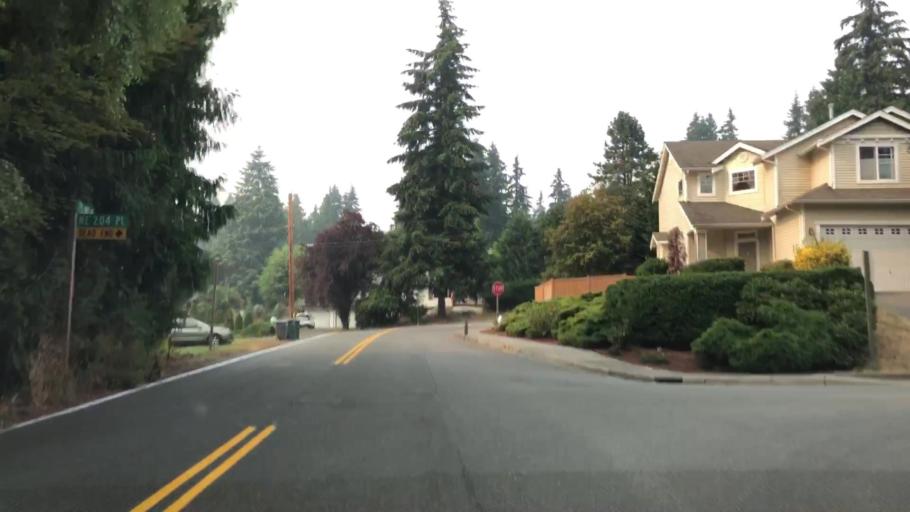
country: US
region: Washington
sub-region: King County
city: Kenmore
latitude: 47.7764
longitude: -122.2409
